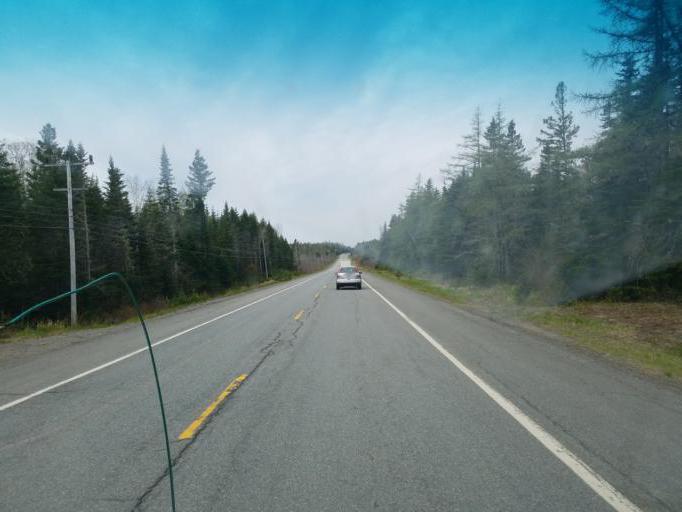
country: US
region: Maine
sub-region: Washington County
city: East Machias
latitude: 44.7537
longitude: -67.2413
